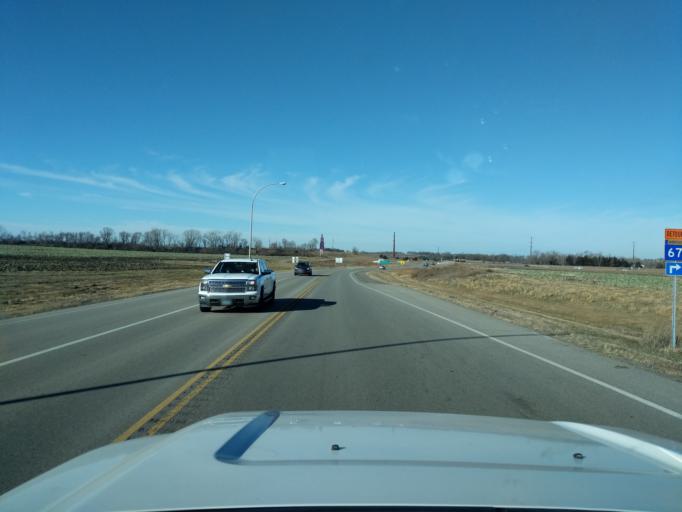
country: US
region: Minnesota
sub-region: Yellow Medicine County
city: Granite Falls
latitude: 44.7705
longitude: -95.5435
